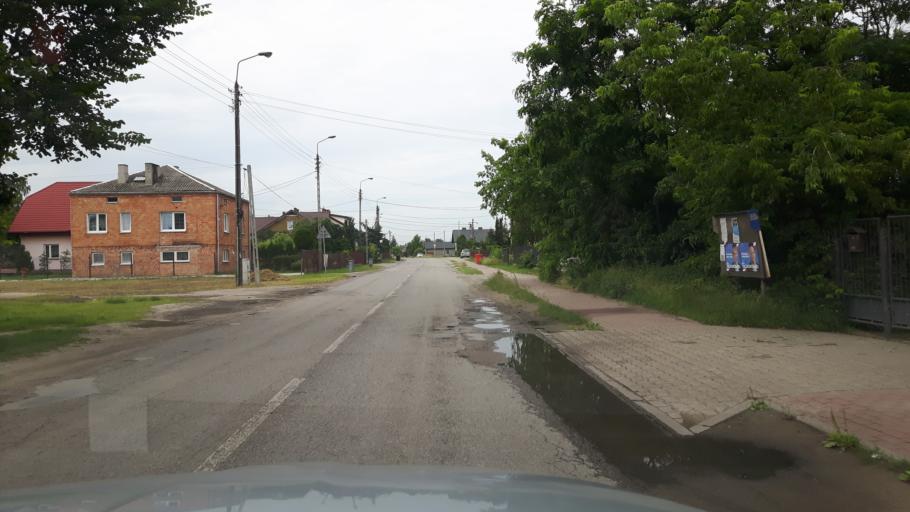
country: PL
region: Masovian Voivodeship
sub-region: Powiat wolominski
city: Kobylka
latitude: 52.3121
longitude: 21.2124
